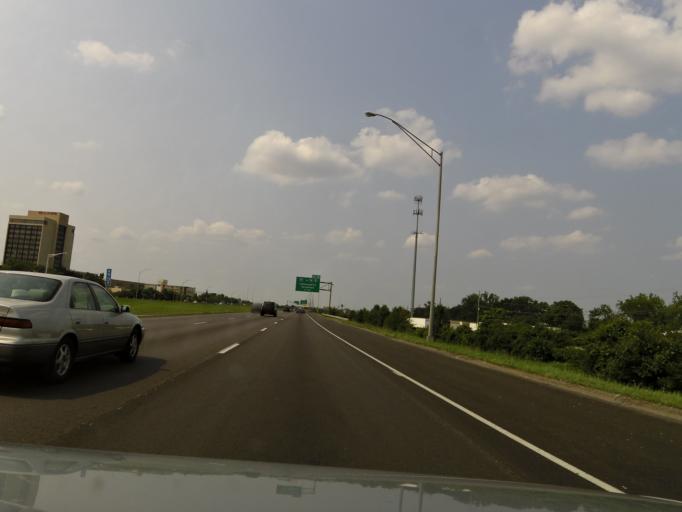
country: US
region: Ohio
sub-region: Hamilton County
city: Glendale
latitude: 39.2769
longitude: -84.4405
